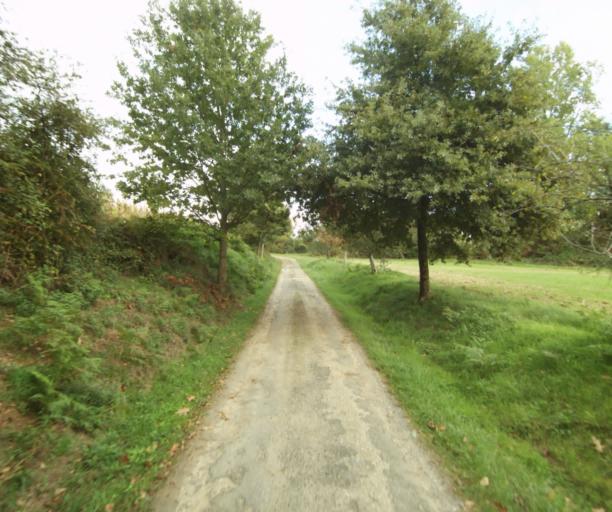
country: FR
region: Midi-Pyrenees
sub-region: Departement du Gers
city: Eauze
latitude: 43.9350
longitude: 0.0784
